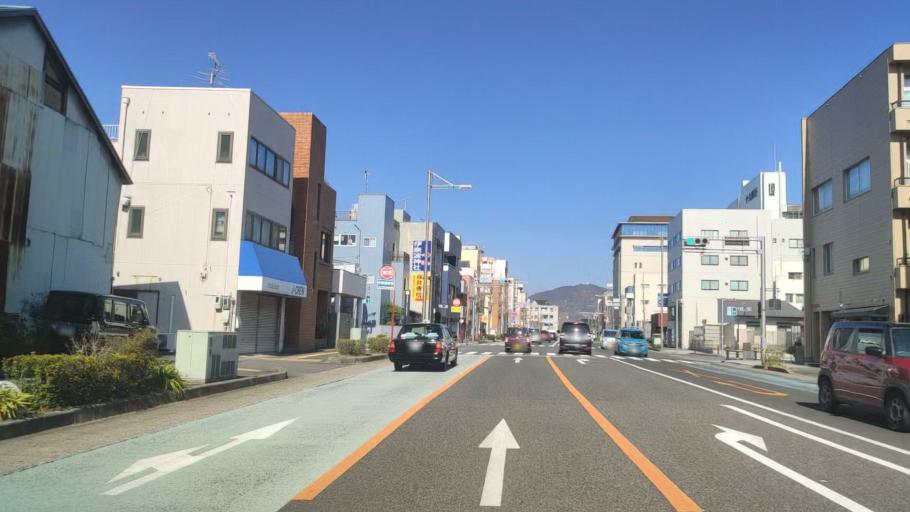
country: JP
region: Gifu
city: Gifu-shi
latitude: 35.4294
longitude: 136.7638
